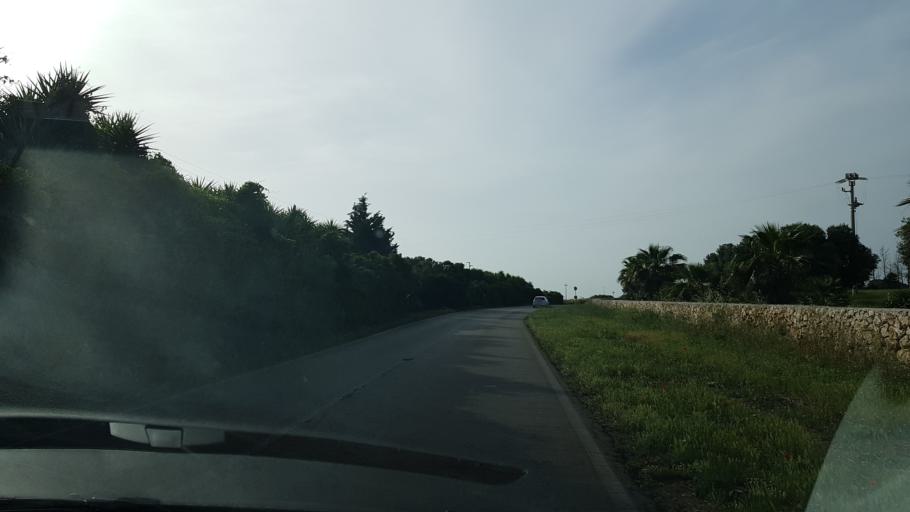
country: IT
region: Apulia
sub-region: Provincia di Lecce
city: Porto Cesareo
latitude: 40.3247
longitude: 17.8543
